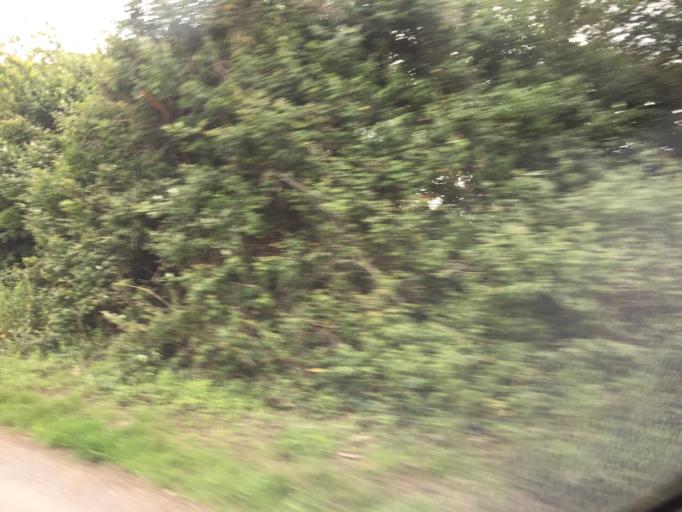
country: GB
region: England
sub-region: South Gloucestershire
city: Horton
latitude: 51.5831
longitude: -2.3460
